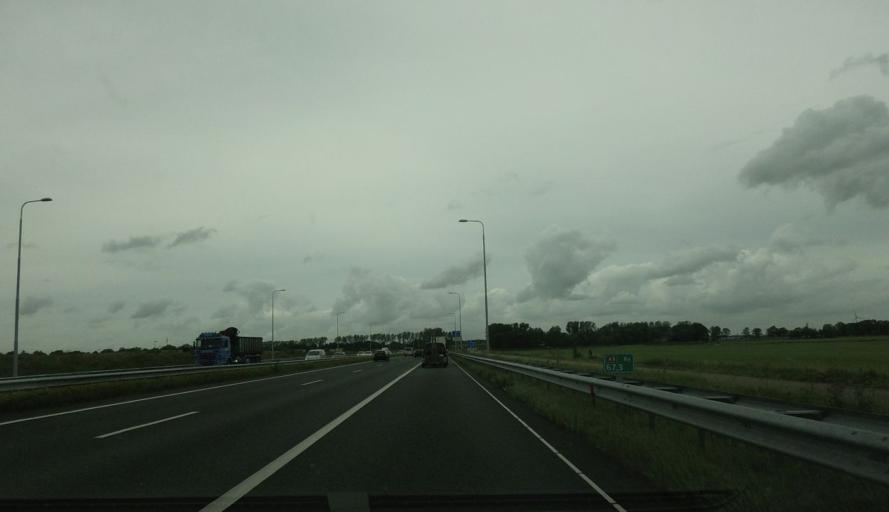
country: NL
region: North Holland
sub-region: Gemeente Heiloo
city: Heiloo
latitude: 52.5889
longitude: 4.7220
